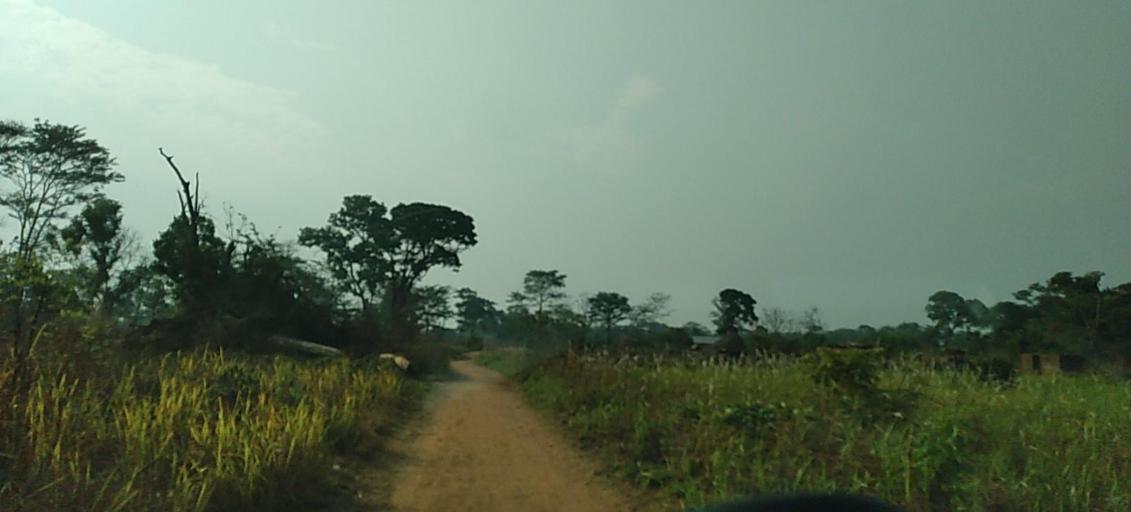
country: ZM
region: North-Western
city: Solwezi
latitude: -12.3661
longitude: 26.5557
